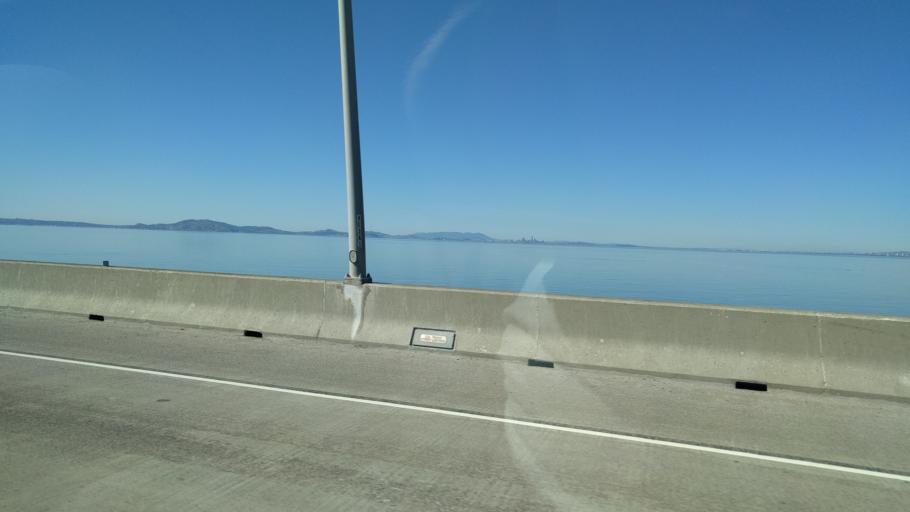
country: US
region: California
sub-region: San Mateo County
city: Foster City
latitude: 37.5976
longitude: -122.2208
